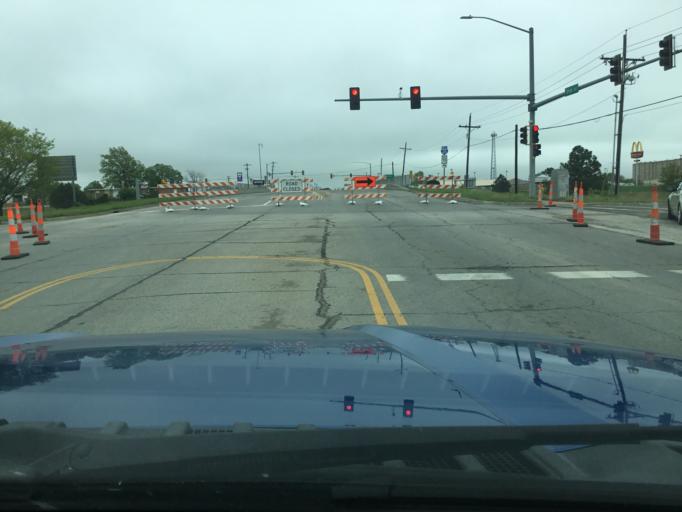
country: US
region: Kansas
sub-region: Shawnee County
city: Topeka
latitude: 39.0291
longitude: -95.7556
